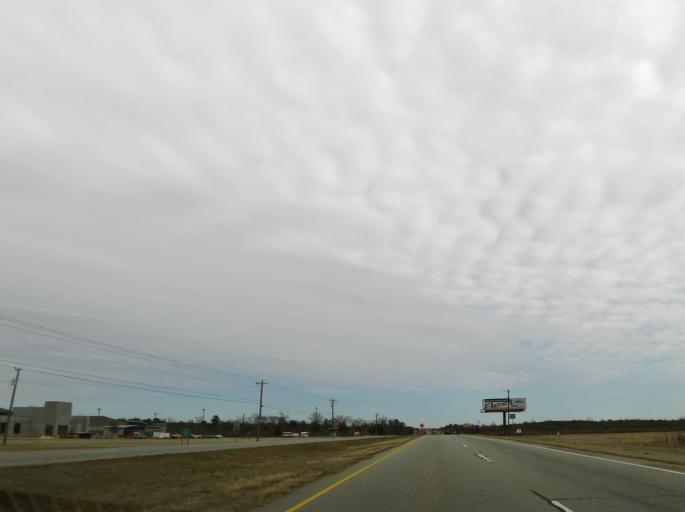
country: US
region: Georgia
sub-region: Houston County
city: Centerville
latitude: 32.6145
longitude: -83.7195
